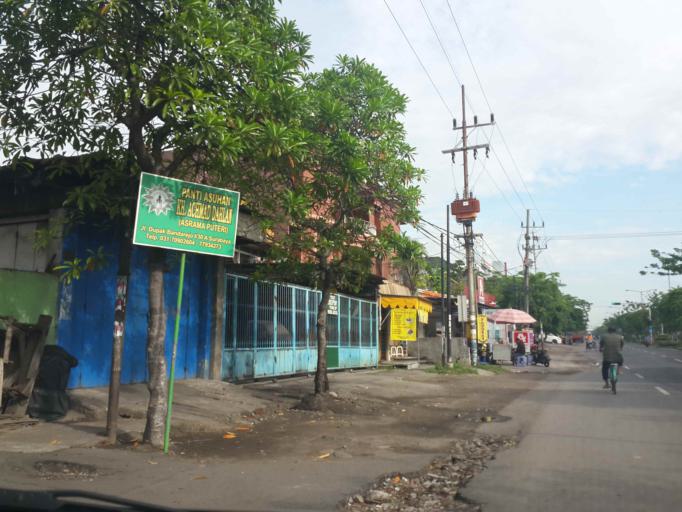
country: ID
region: East Java
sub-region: Kota Surabaya
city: Surabaya
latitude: -7.2431
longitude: 112.7208
